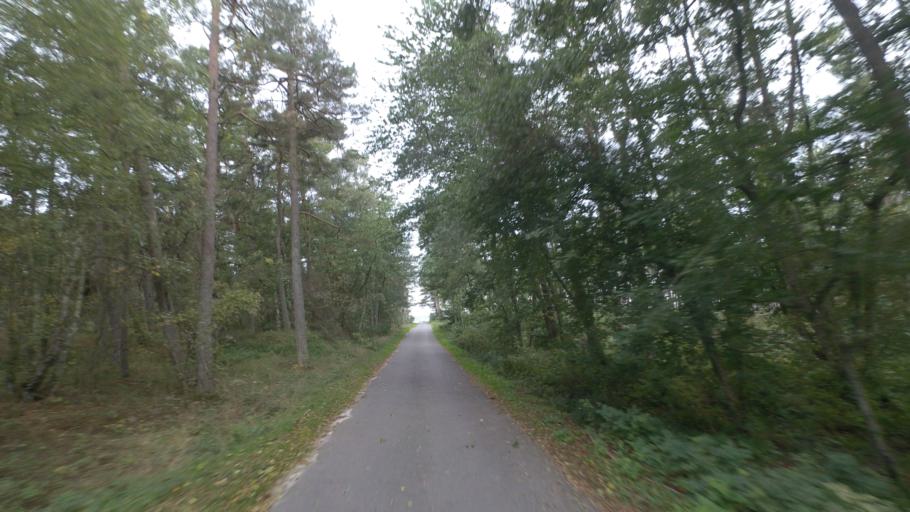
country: DK
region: Capital Region
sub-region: Bornholm Kommune
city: Nexo
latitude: 54.9971
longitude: 15.0385
